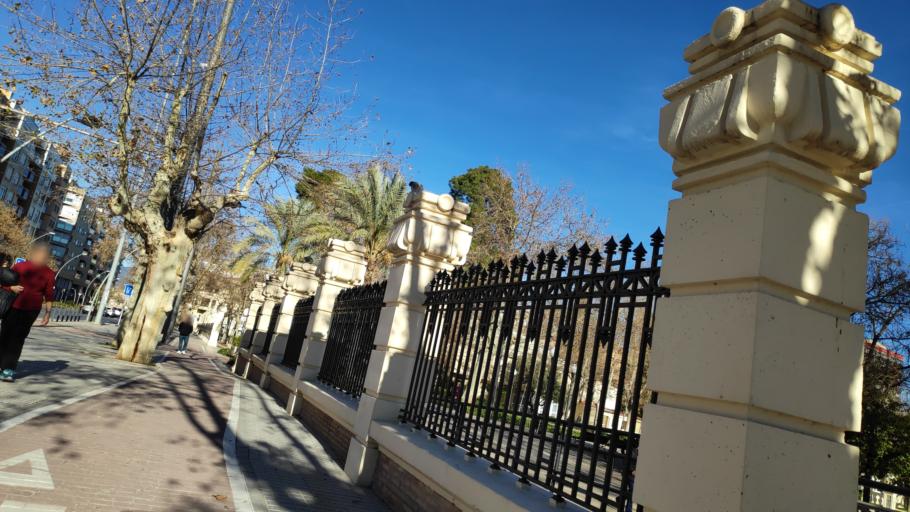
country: ES
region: Valencia
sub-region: Provincia de Castello
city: Castello de la Plana
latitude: 39.9883
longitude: -0.0467
